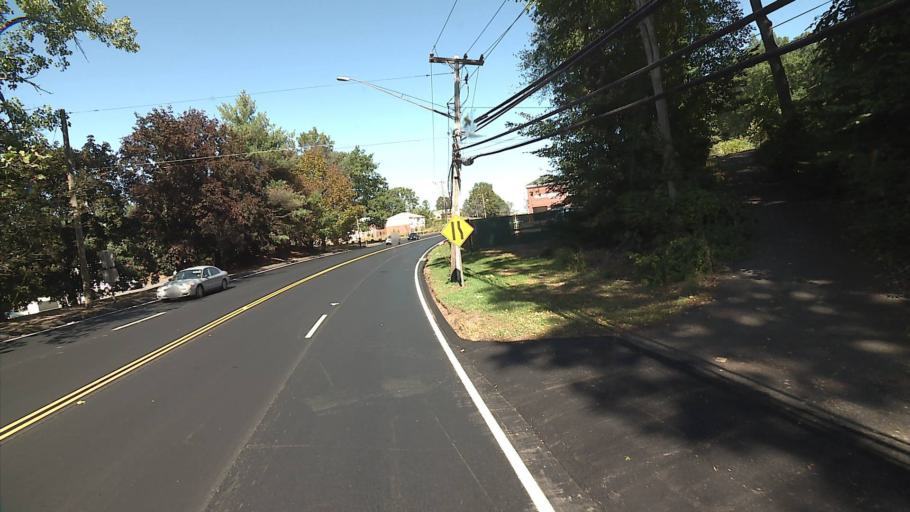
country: US
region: Connecticut
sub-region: Tolland County
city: Rockville
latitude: 41.8587
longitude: -72.4848
